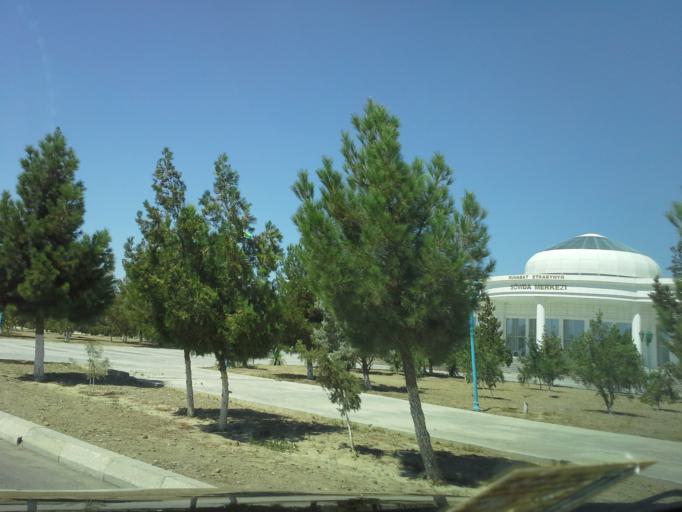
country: TM
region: Ahal
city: Ashgabat
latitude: 37.9885
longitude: 58.3271
